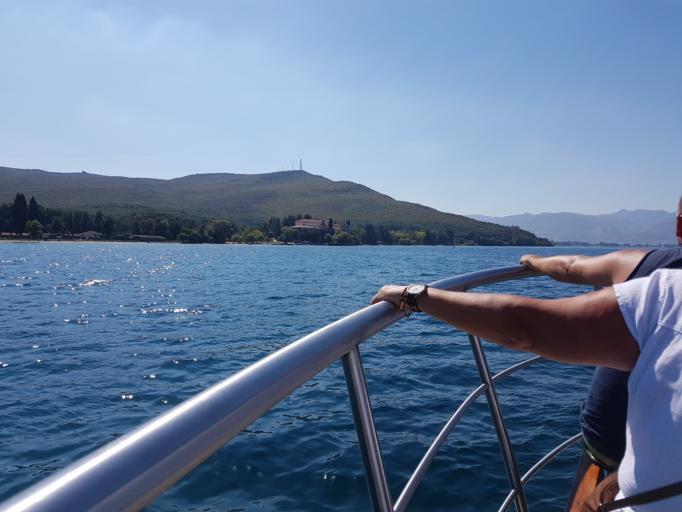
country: AL
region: Korce
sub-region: Rrethi i Pogradecit
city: Bucimas
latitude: 40.9186
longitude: 20.7441
